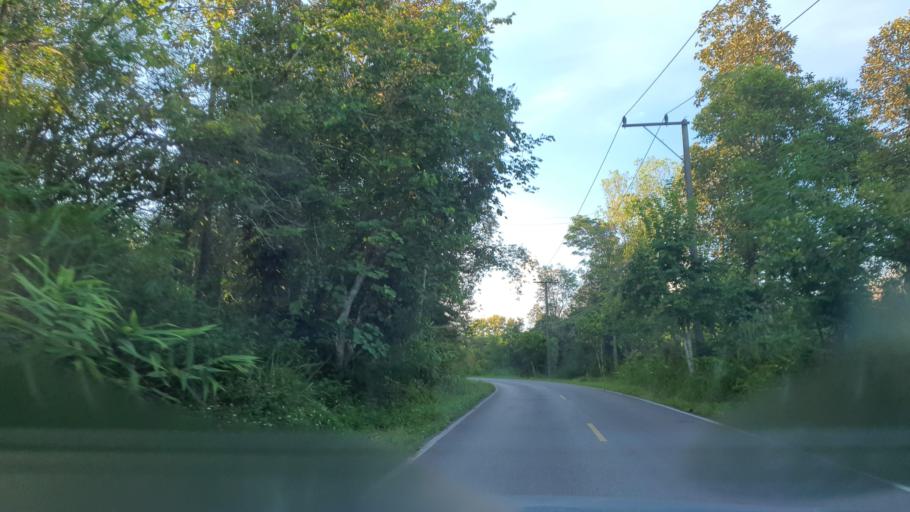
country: TH
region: Chiang Mai
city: Mae On
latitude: 18.8427
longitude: 99.2800
